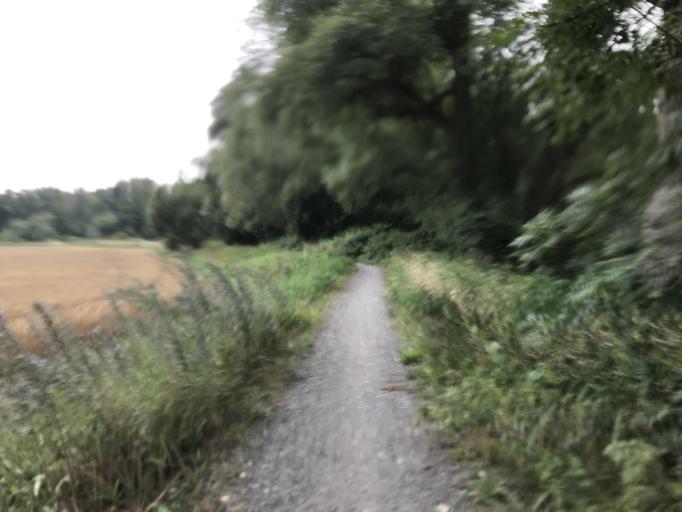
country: DE
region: Saxony-Anhalt
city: Weddersleben
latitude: 51.7672
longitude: 11.1014
